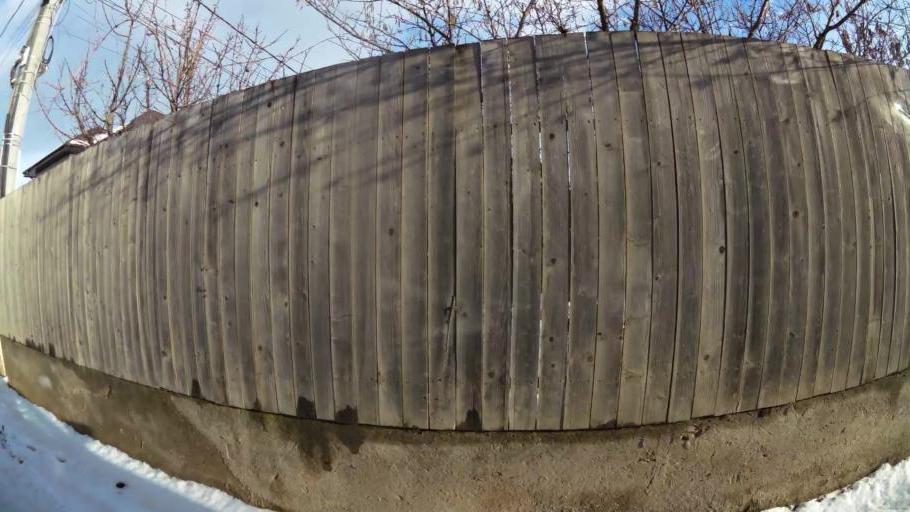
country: RO
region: Ilfov
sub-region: Comuna Fundeni-Dobroesti
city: Fundeni
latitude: 44.4626
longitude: 26.1751
